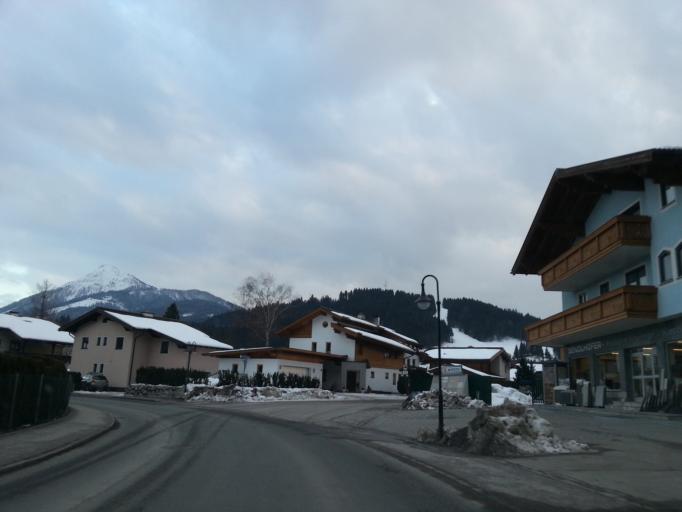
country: AT
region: Salzburg
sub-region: Politischer Bezirk Sankt Johann im Pongau
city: Altenmarkt im Pongau
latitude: 47.3846
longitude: 13.4141
